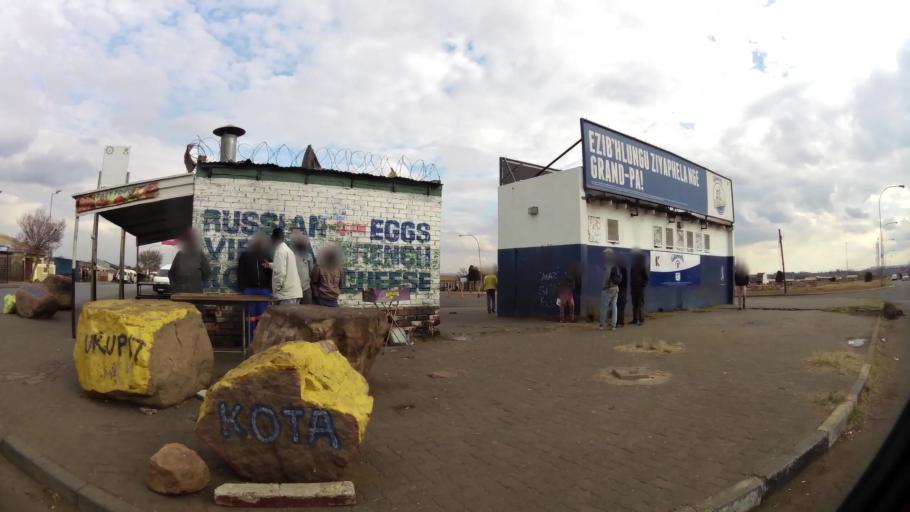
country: ZA
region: Gauteng
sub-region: City of Johannesburg Metropolitan Municipality
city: Soweto
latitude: -26.2467
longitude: 27.8182
